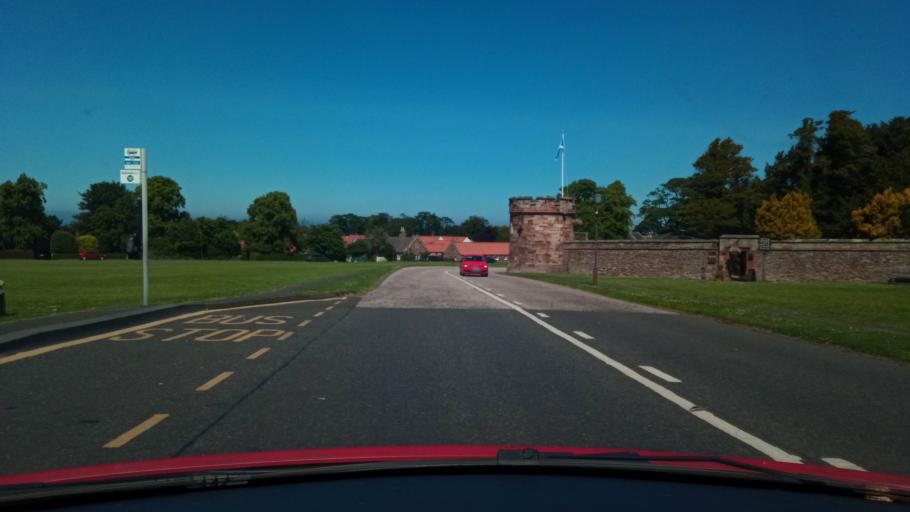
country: GB
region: Scotland
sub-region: East Lothian
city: Gullane
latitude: 56.0457
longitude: -2.7814
